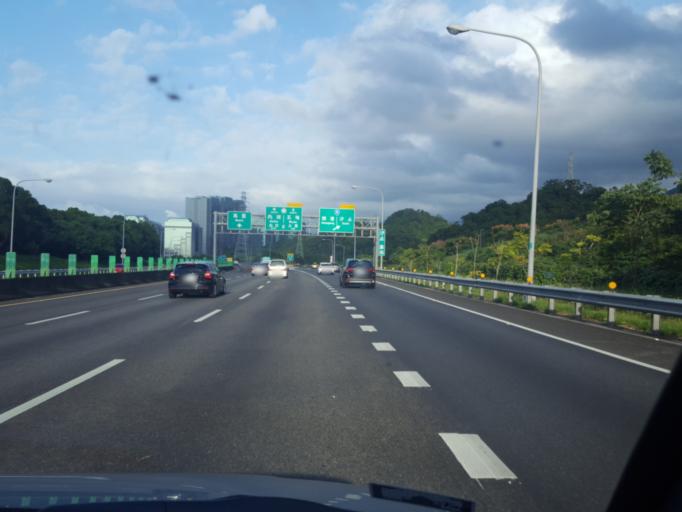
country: TW
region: Taipei
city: Taipei
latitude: 25.0536
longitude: 121.6351
